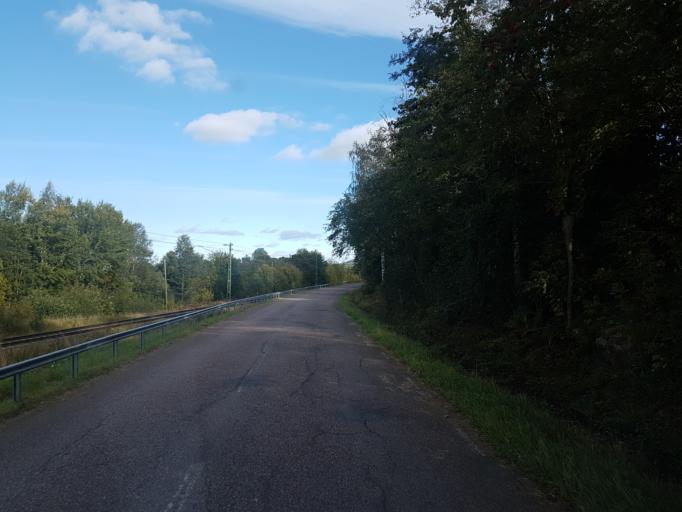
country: SE
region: Dalarna
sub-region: Saters Kommun
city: Saeter
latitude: 60.3643
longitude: 15.7256
